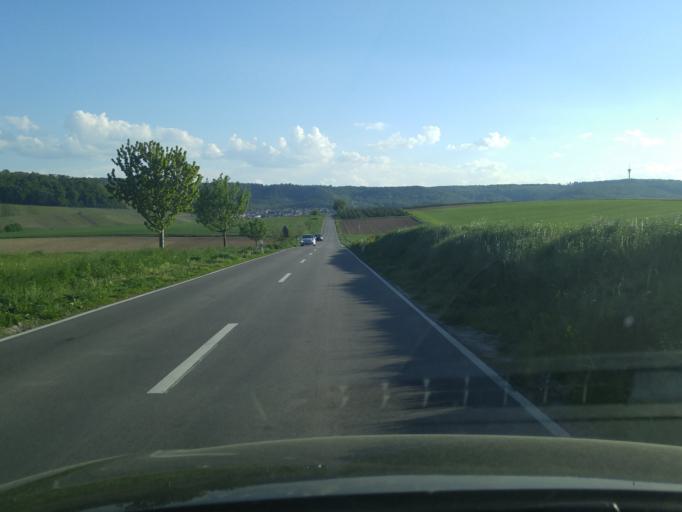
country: DE
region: Baden-Wuerttemberg
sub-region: Regierungsbezirk Stuttgart
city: Cleebronn
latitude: 49.0574
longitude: 9.0490
